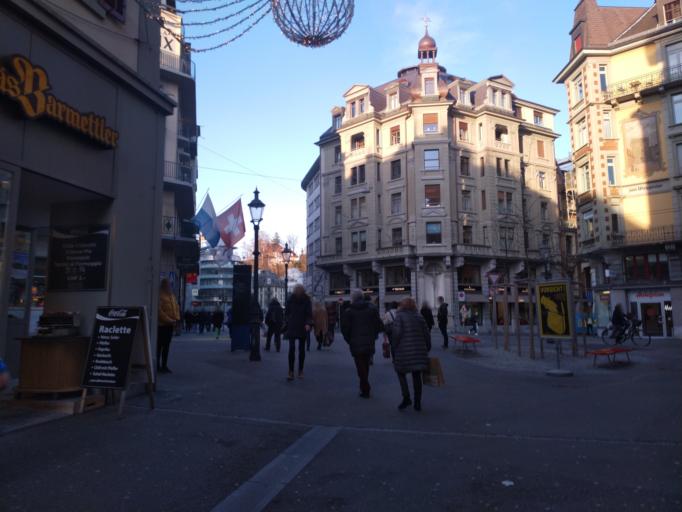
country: CH
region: Lucerne
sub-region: Lucerne-Stadt District
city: Luzern
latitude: 47.0555
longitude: 8.3104
